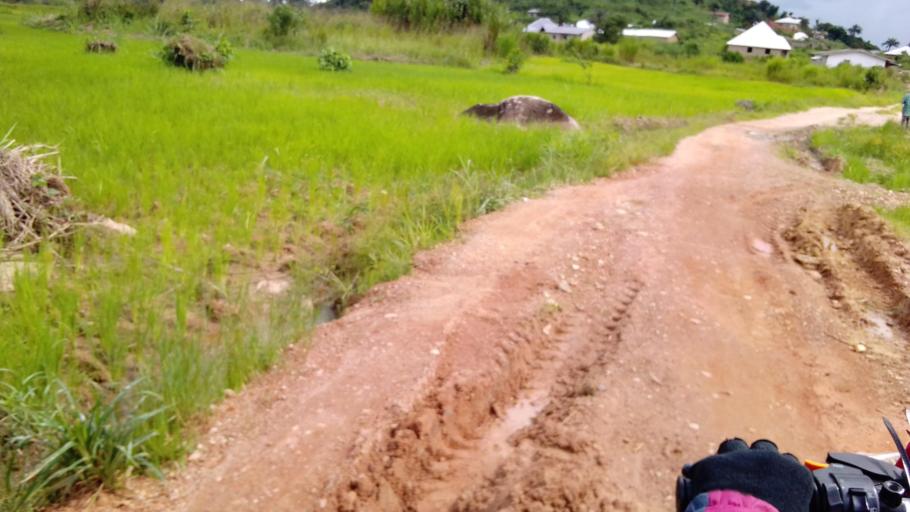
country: SL
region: Eastern Province
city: Koidu
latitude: 8.6694
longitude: -10.9798
